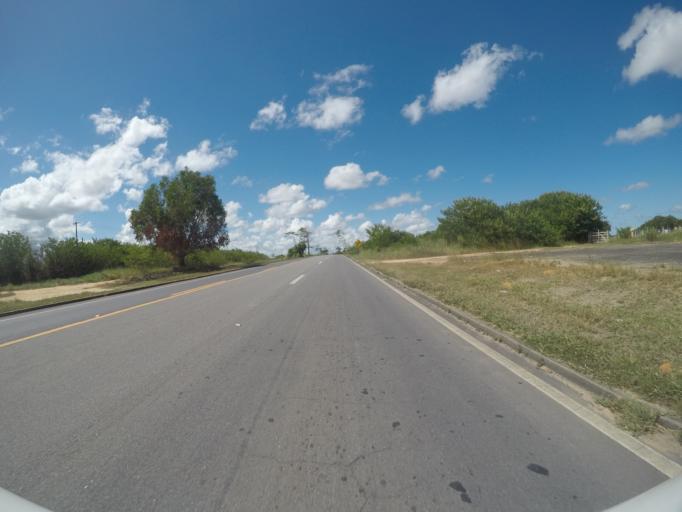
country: BR
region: Espirito Santo
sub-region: Conceicao Da Barra
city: Conceicao da Barra
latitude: -18.2737
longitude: -39.9598
